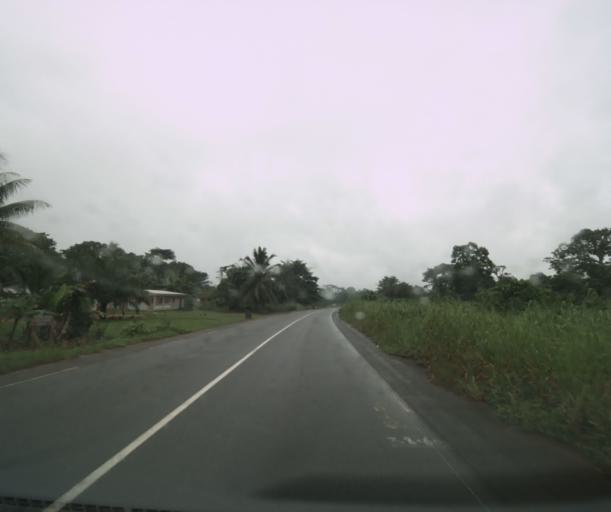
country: CM
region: Littoral
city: Edea
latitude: 3.4715
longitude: 10.1339
